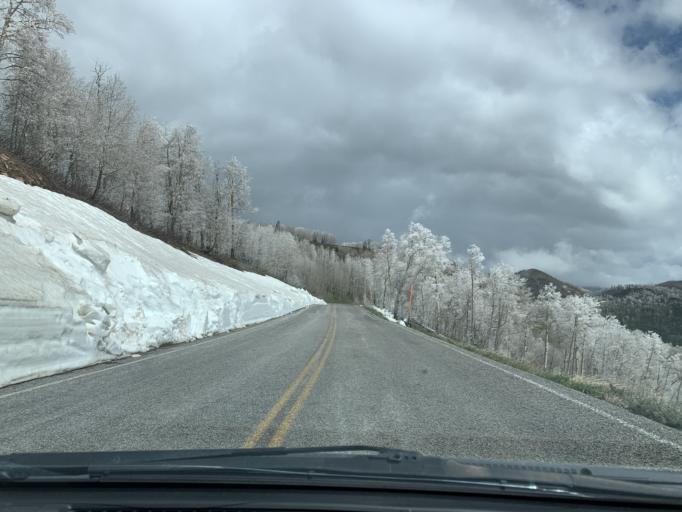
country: US
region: Utah
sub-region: Utah County
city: Santaquin
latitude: 39.8502
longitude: -111.7031
